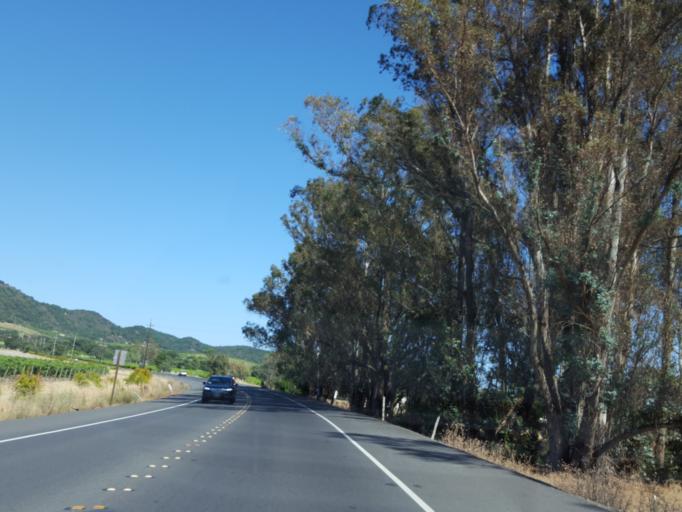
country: US
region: California
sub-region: Sonoma County
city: Sonoma
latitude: 38.2708
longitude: -122.4219
